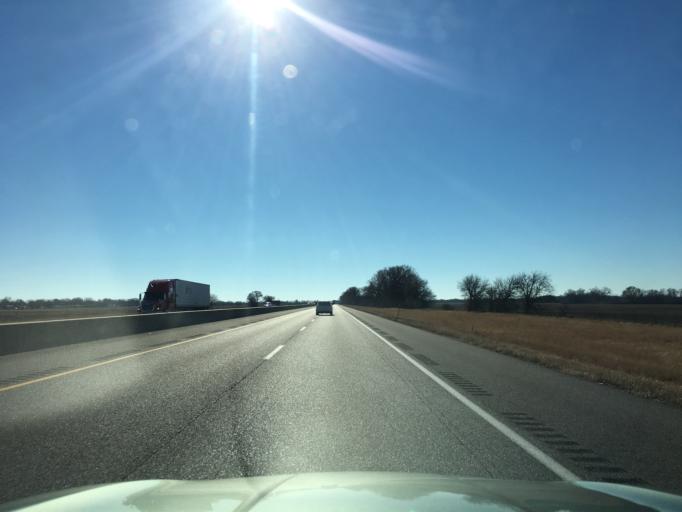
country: US
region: Kansas
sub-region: Sumner County
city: Belle Plaine
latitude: 37.4486
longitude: -97.3222
